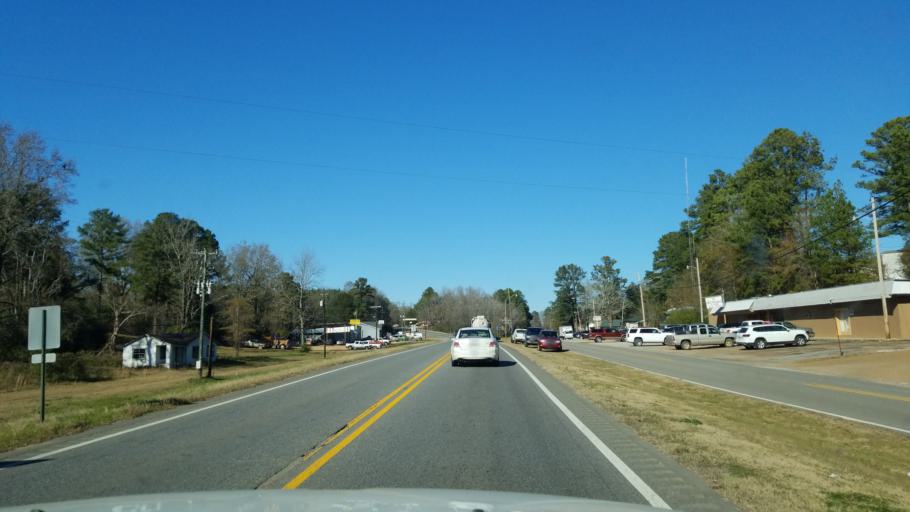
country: US
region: Alabama
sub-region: Pickens County
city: Gordo
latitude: 33.3260
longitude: -87.9109
